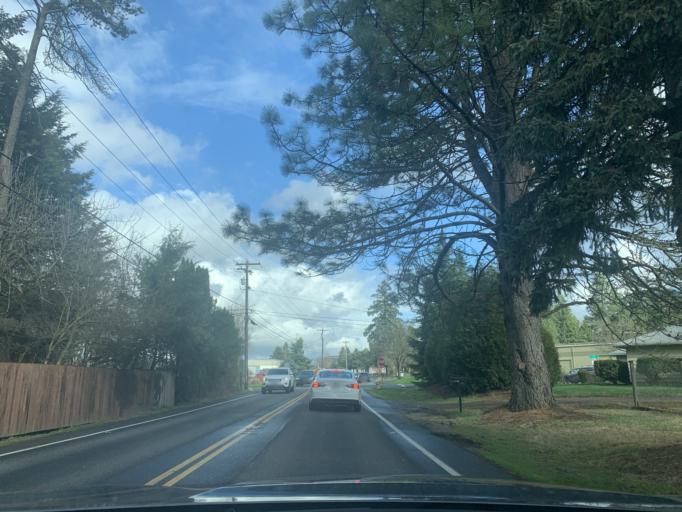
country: US
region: Oregon
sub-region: Washington County
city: Tigard
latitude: 45.4358
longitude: -122.7833
